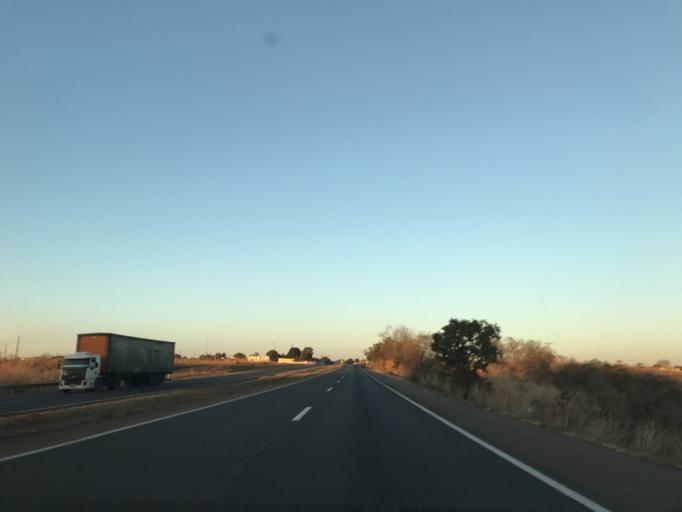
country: BR
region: Goias
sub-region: Abadiania
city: Abadiania
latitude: -16.1873
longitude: -48.6995
